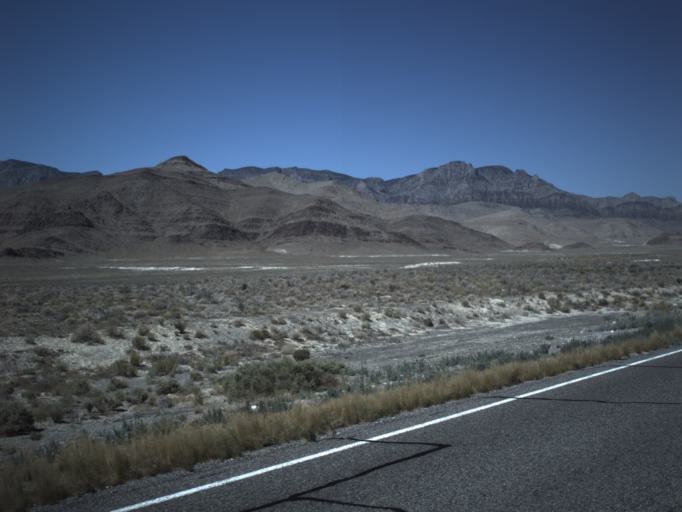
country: US
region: Utah
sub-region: Beaver County
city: Milford
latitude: 39.0350
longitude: -113.3902
